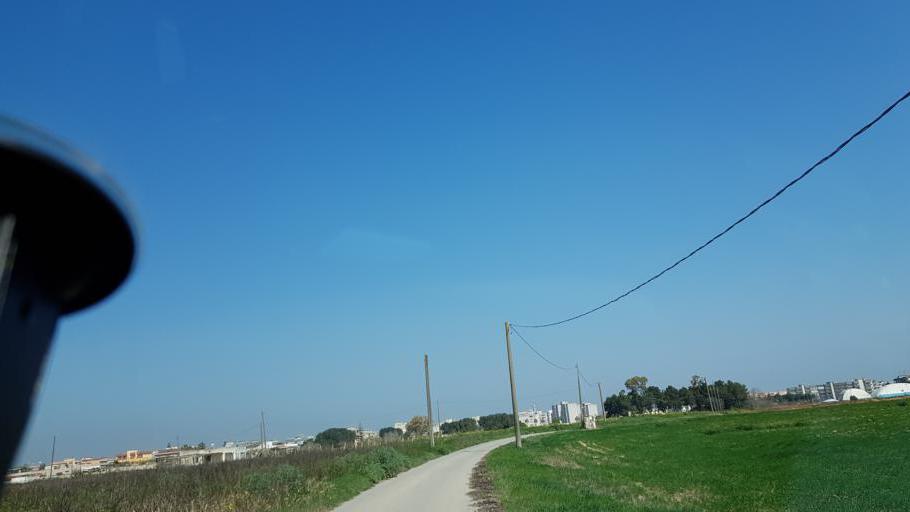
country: IT
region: Apulia
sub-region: Provincia di Brindisi
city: Brindisi
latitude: 40.6107
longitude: 17.9293
